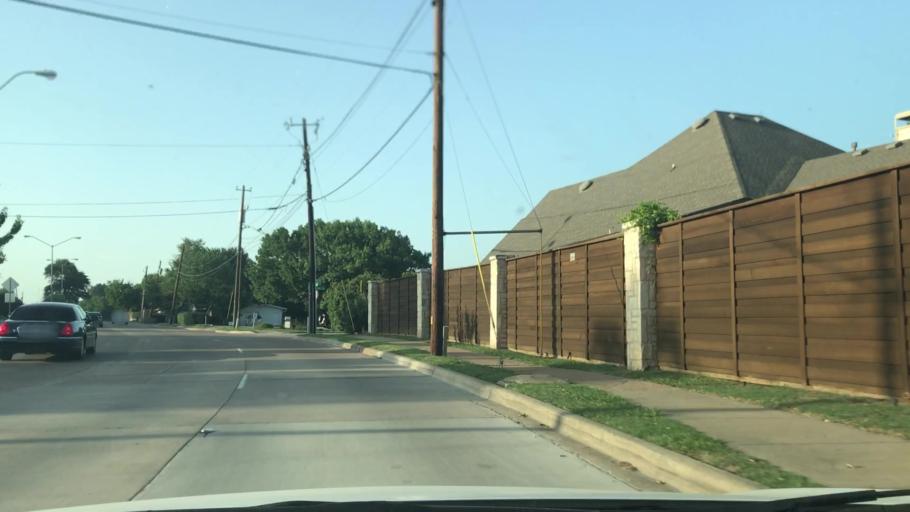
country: US
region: Texas
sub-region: Dallas County
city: Garland
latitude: 32.8718
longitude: -96.7000
